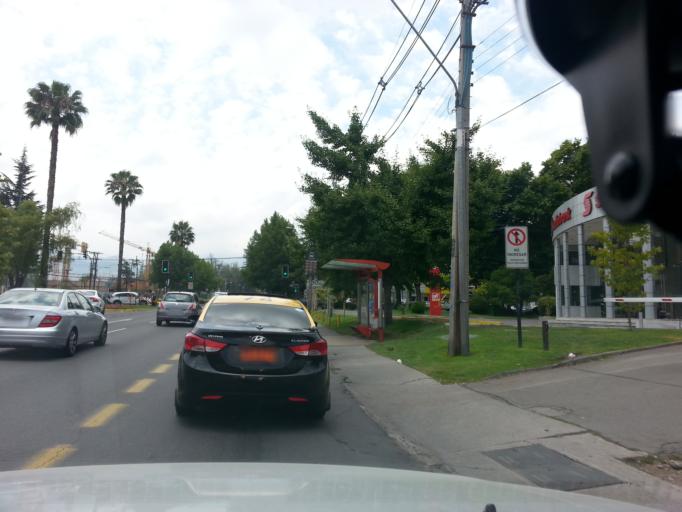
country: CL
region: Santiago Metropolitan
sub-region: Provincia de Santiago
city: Villa Presidente Frei, Nunoa, Santiago, Chile
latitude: -33.3767
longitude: -70.5264
